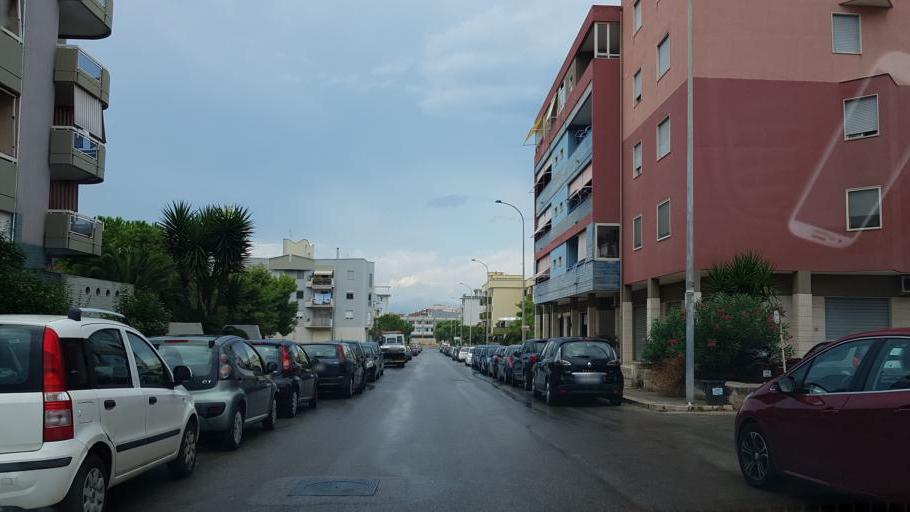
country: IT
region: Apulia
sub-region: Provincia di Bari
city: Monopoli
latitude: 40.9439
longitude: 17.3087
